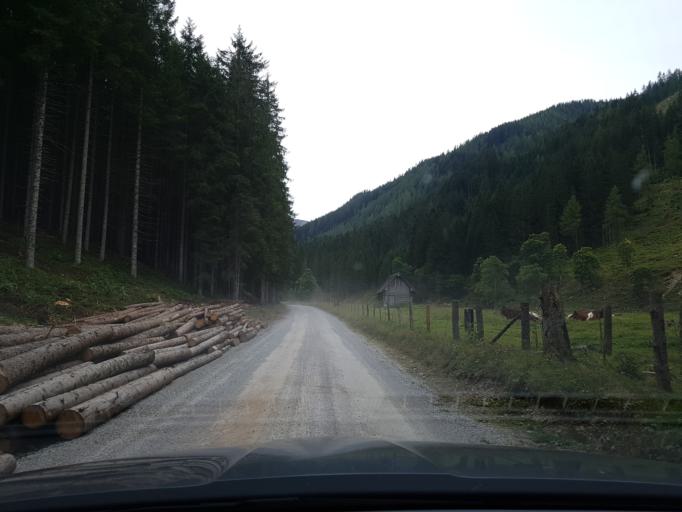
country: AT
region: Salzburg
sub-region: Politischer Bezirk Sankt Johann im Pongau
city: Forstau
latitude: 47.3235
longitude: 13.5779
